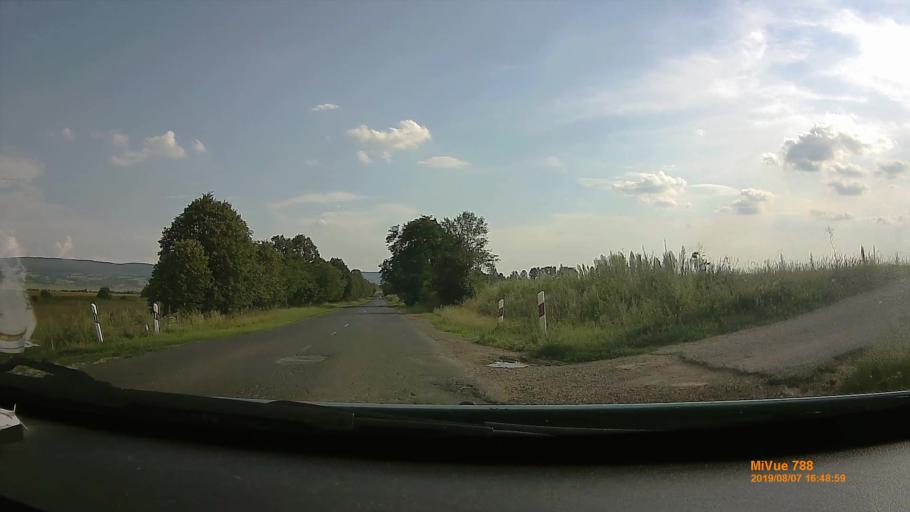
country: HU
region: Borsod-Abauj-Zemplen
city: Abaujszanto
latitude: 48.3253
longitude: 21.2013
